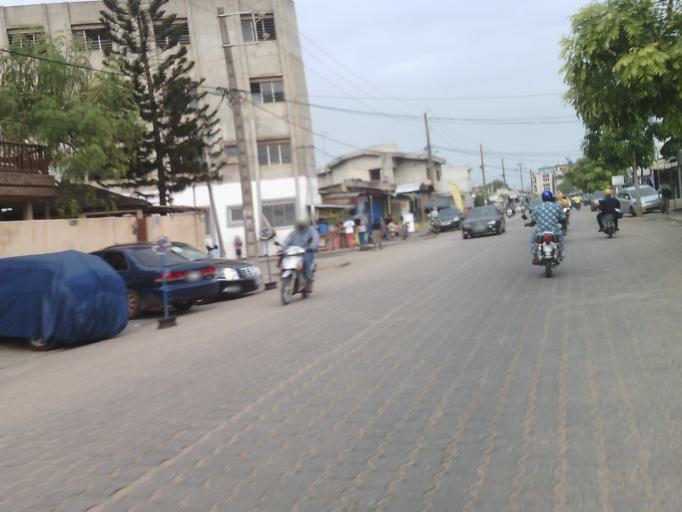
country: BJ
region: Littoral
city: Cotonou
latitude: 6.3869
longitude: 2.3816
